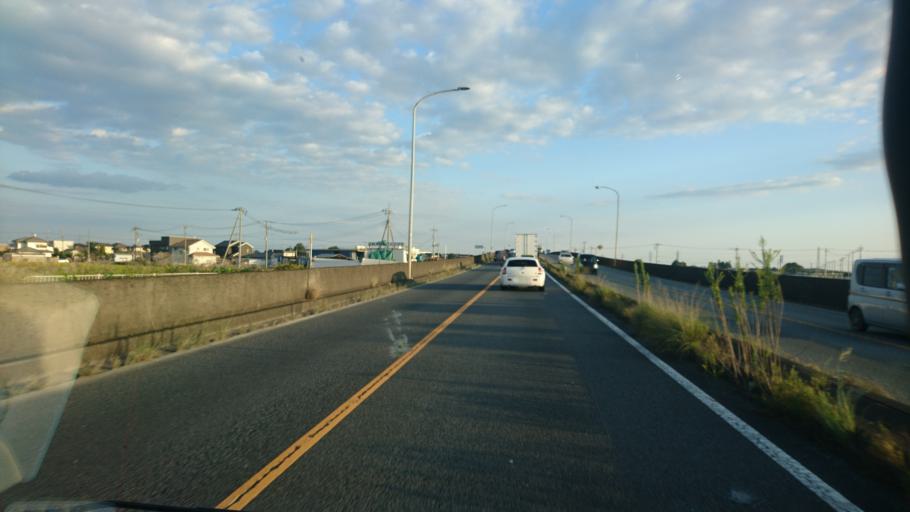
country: JP
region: Gunma
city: Ota
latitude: 36.3408
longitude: 139.3859
